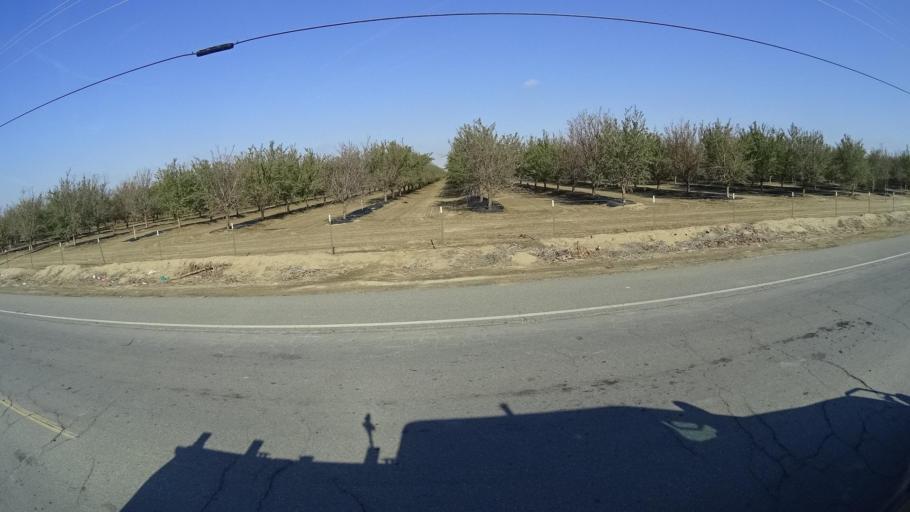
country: US
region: California
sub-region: Kern County
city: Arvin
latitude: 35.1952
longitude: -118.8457
